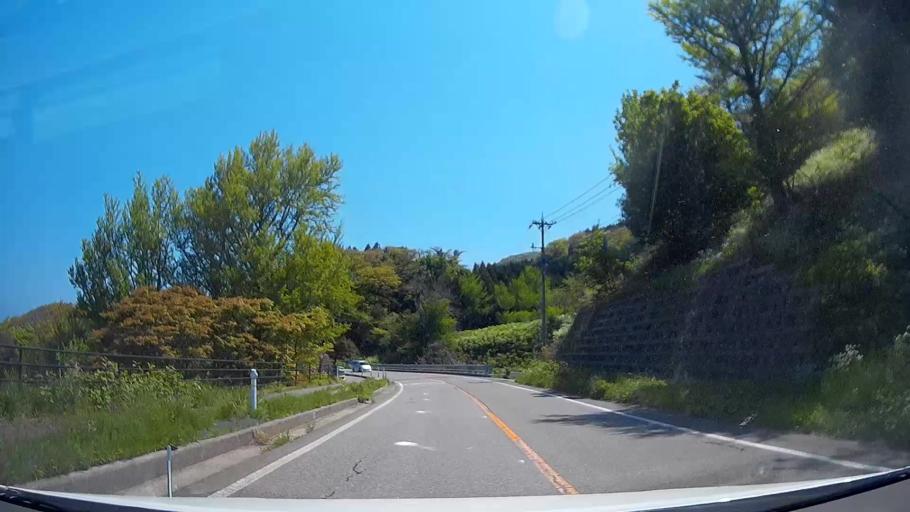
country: JP
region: Ishikawa
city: Nanao
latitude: 37.4203
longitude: 136.9887
